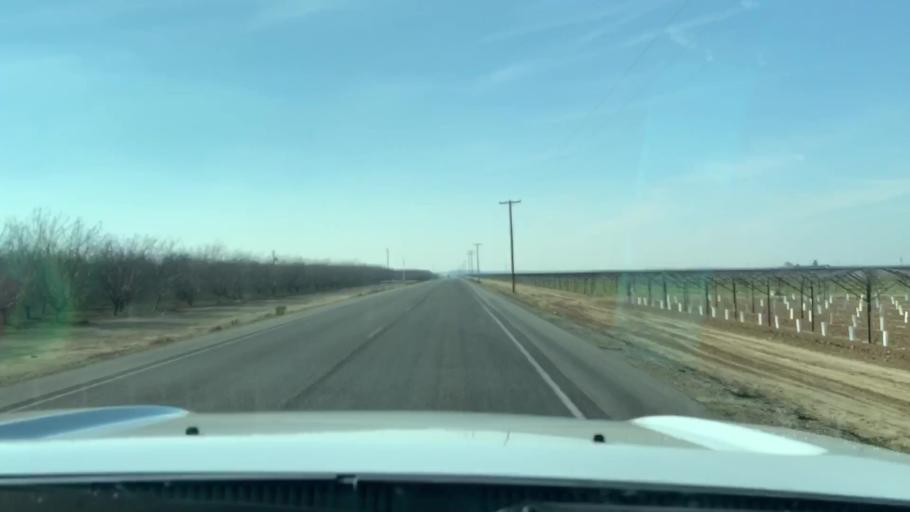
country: US
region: California
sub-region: Kern County
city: Buttonwillow
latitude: 35.5005
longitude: -119.4272
